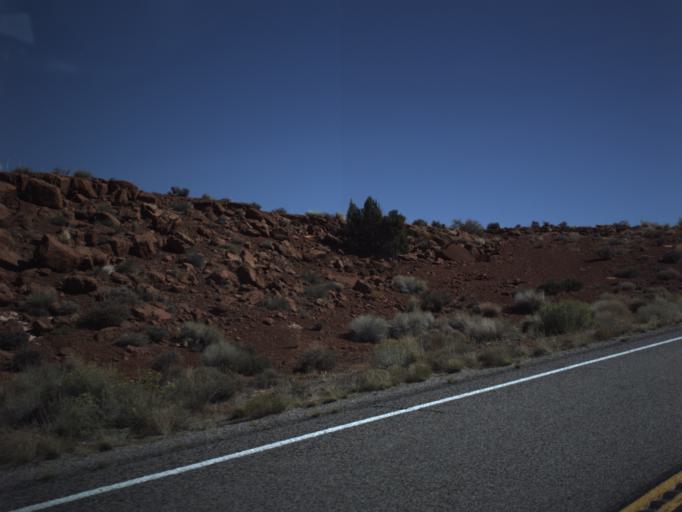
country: US
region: Utah
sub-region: San Juan County
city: Blanding
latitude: 37.8102
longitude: -110.3334
